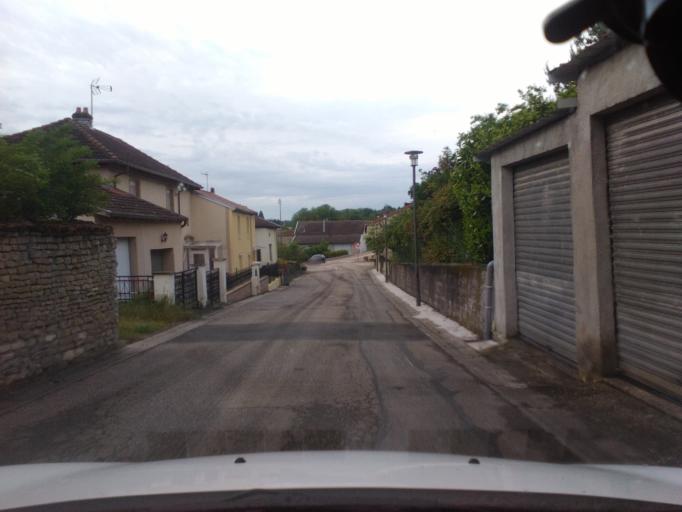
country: FR
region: Lorraine
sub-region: Departement des Vosges
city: Mirecourt
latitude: 48.3207
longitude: 6.1254
